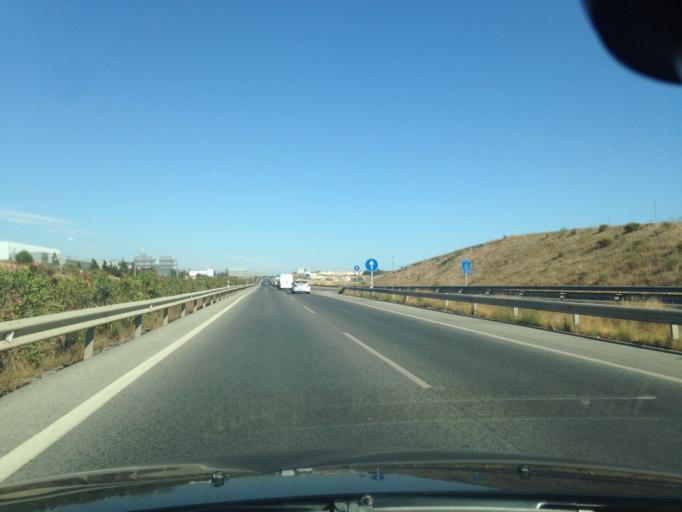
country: ES
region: Andalusia
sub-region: Provincia de Malaga
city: Alhaurin de la Torre
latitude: 36.7134
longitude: -4.5018
